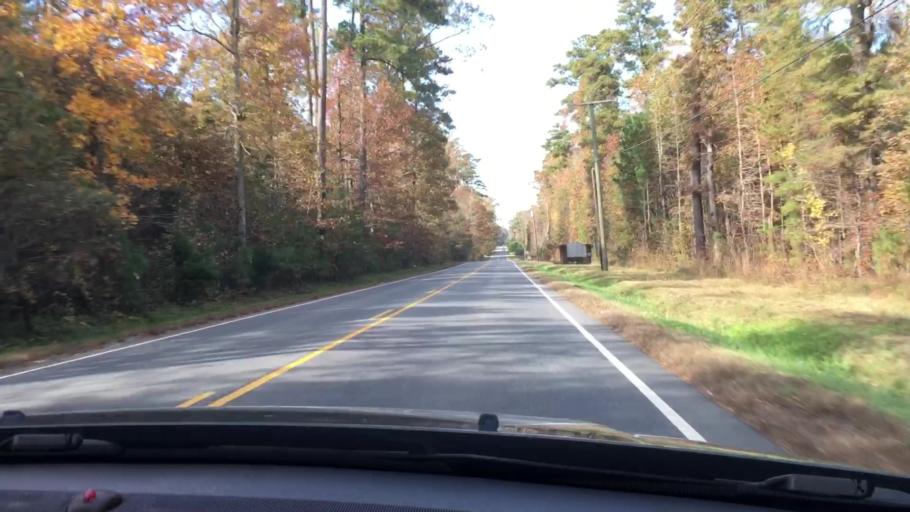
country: US
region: Virginia
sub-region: King William County
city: West Point
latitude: 37.5671
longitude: -76.8311
